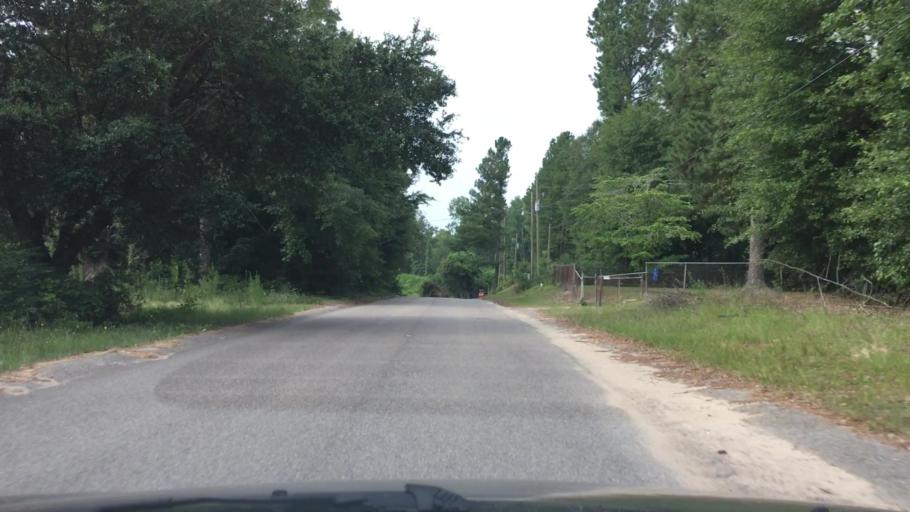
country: US
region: South Carolina
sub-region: Barnwell County
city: Williston
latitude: 33.6560
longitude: -81.3725
